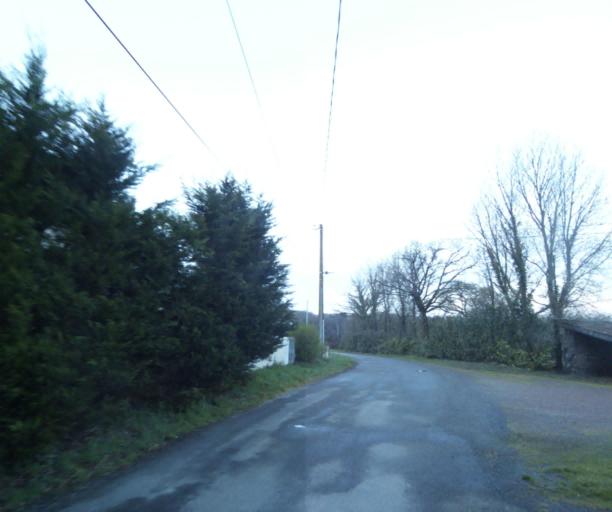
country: FR
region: Pays de la Loire
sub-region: Departement de la Loire-Atlantique
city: Malville
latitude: 47.3773
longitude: -1.8975
